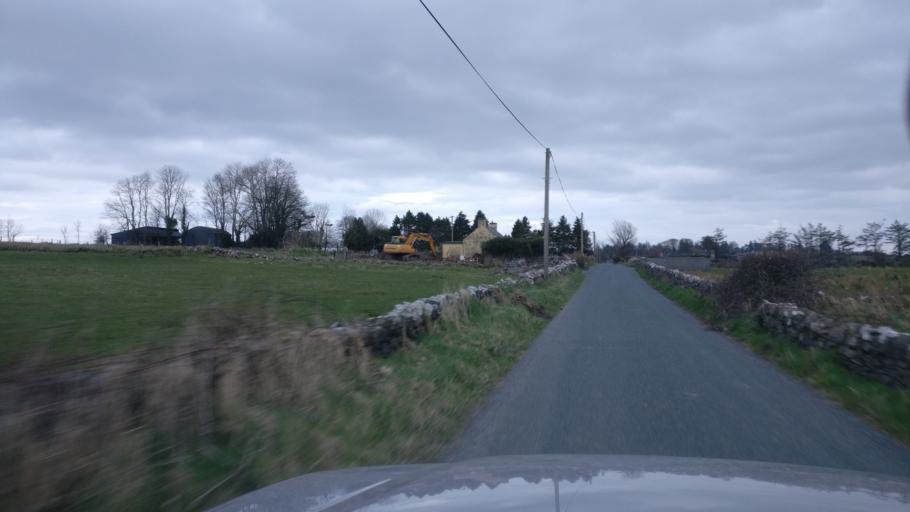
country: IE
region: Connaught
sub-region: County Galway
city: Loughrea
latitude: 53.2674
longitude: -8.4881
